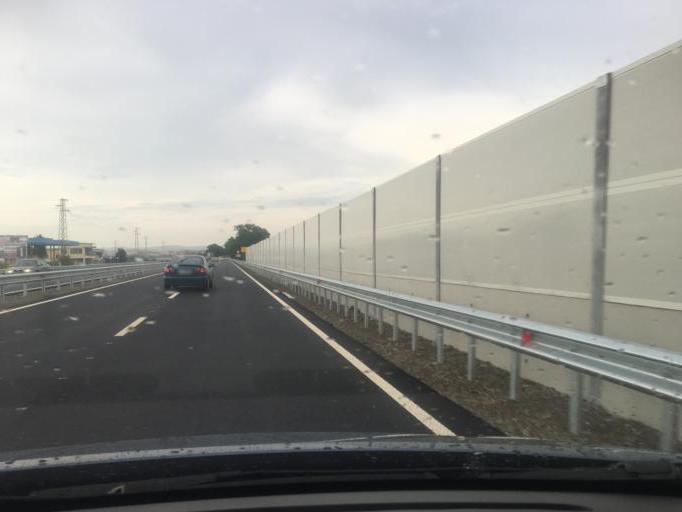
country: BG
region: Burgas
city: Aheloy
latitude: 42.6354
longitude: 27.6370
